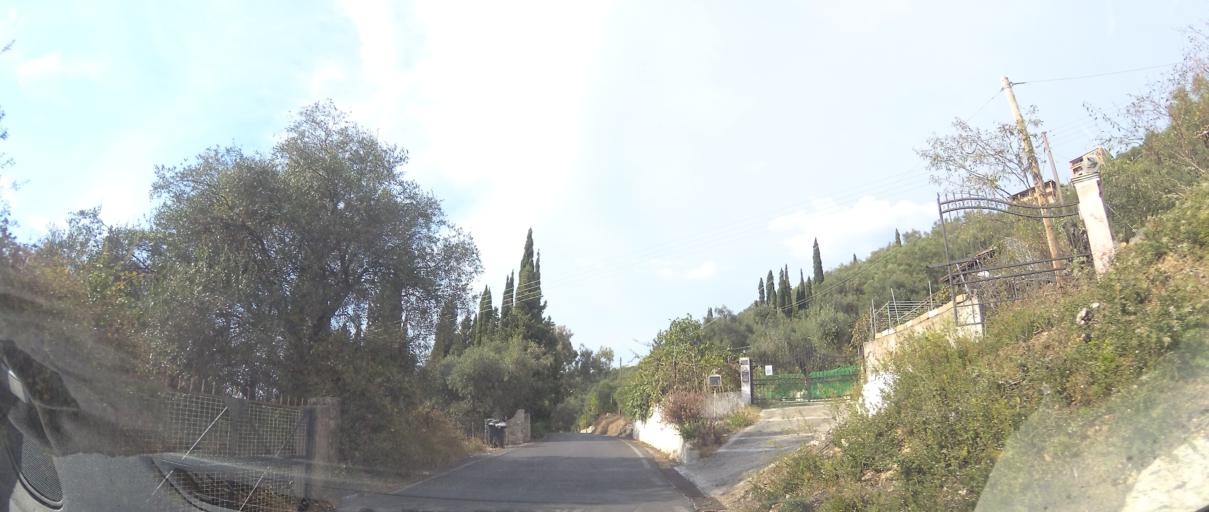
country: GR
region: Ionian Islands
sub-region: Nomos Kerkyras
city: Kynopiastes
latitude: 39.5480
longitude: 19.8670
